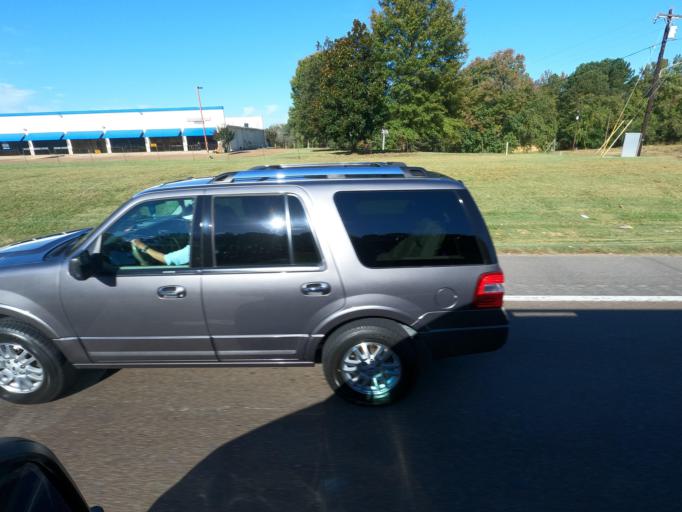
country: US
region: Tennessee
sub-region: Tipton County
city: Brighton
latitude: 35.4831
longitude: -89.7399
